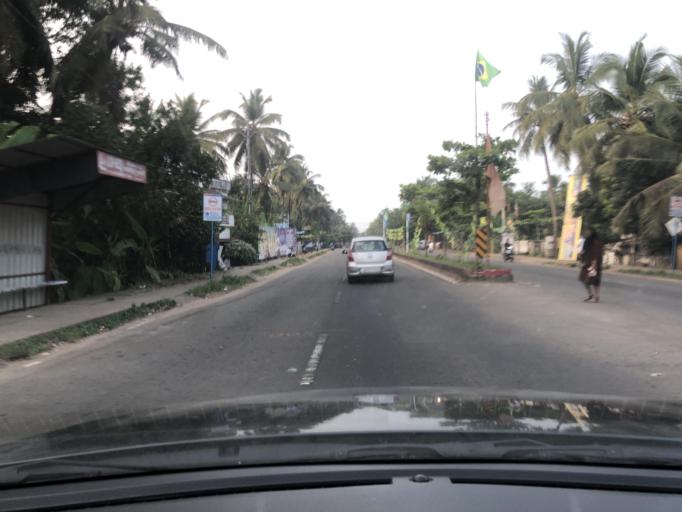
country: IN
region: Kerala
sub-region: Kozhikode
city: Kozhikode
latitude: 11.2955
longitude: 75.7569
